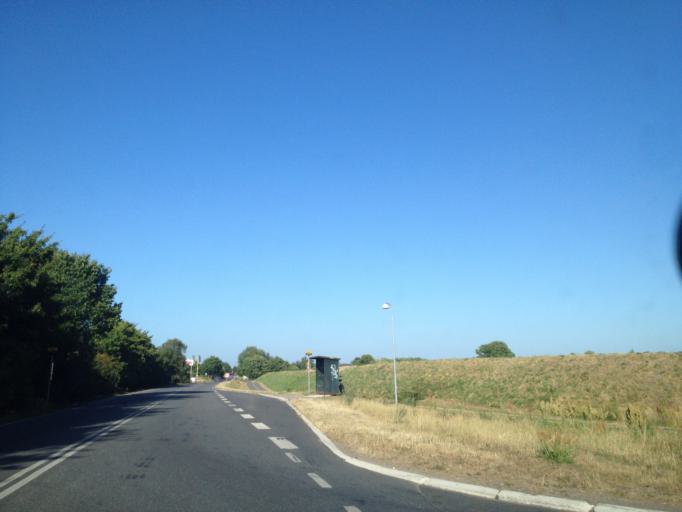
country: DK
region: Capital Region
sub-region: Gribskov Kommune
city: Helsinge
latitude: 56.0162
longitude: 12.1616
